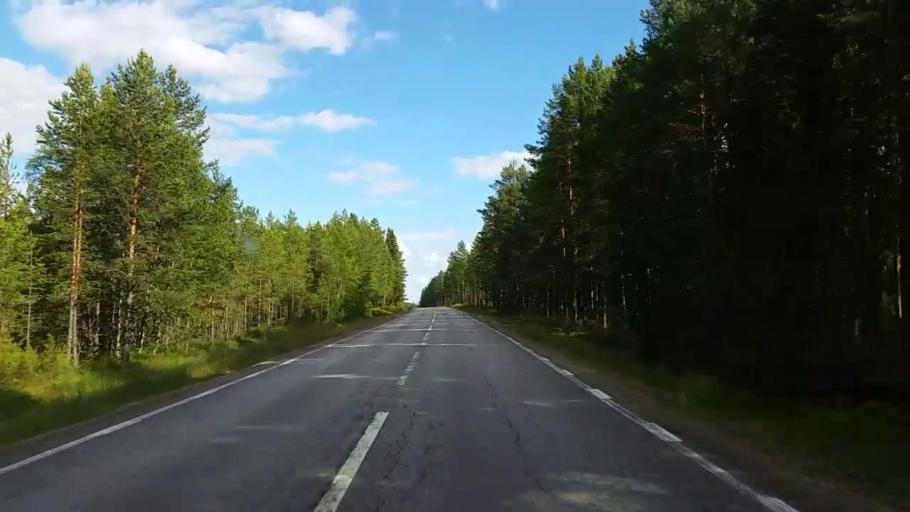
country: SE
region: Gaevleborg
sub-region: Ljusdals Kommun
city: Farila
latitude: 62.0919
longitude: 15.8007
